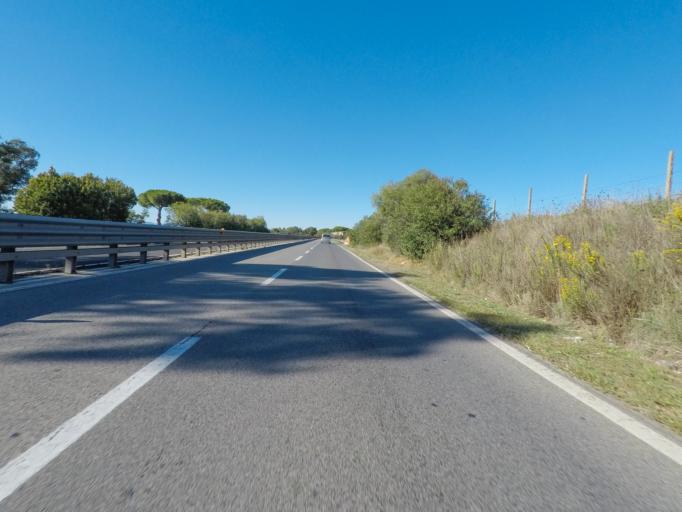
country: IT
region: Tuscany
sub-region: Provincia di Grosseto
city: Grosseto
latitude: 42.7202
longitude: 11.1399
